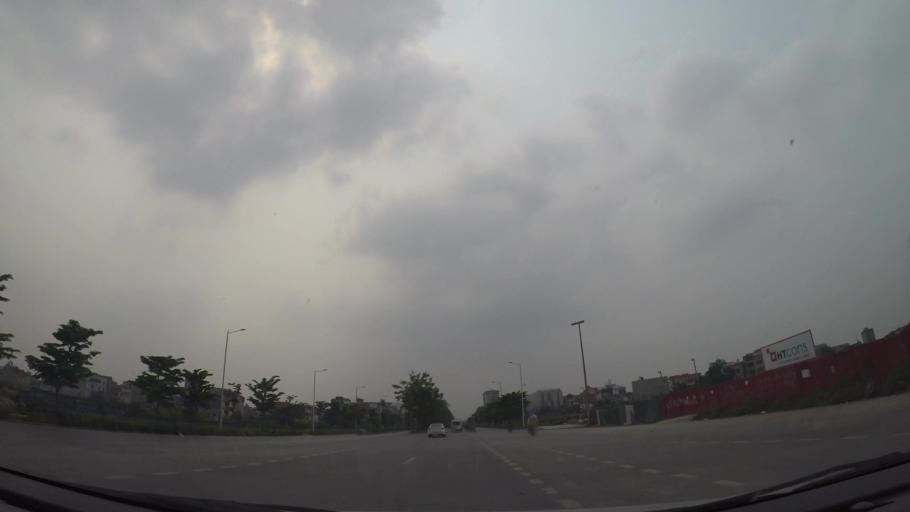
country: VN
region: Ha Noi
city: Cau Dien
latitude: 21.0380
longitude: 105.7460
